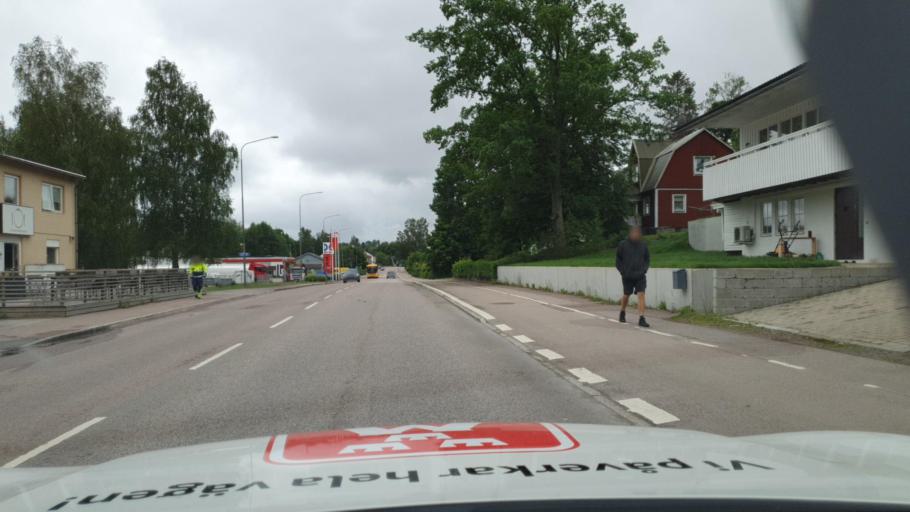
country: SE
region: Vaermland
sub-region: Grums Kommun
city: Grums
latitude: 59.3595
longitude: 13.1122
